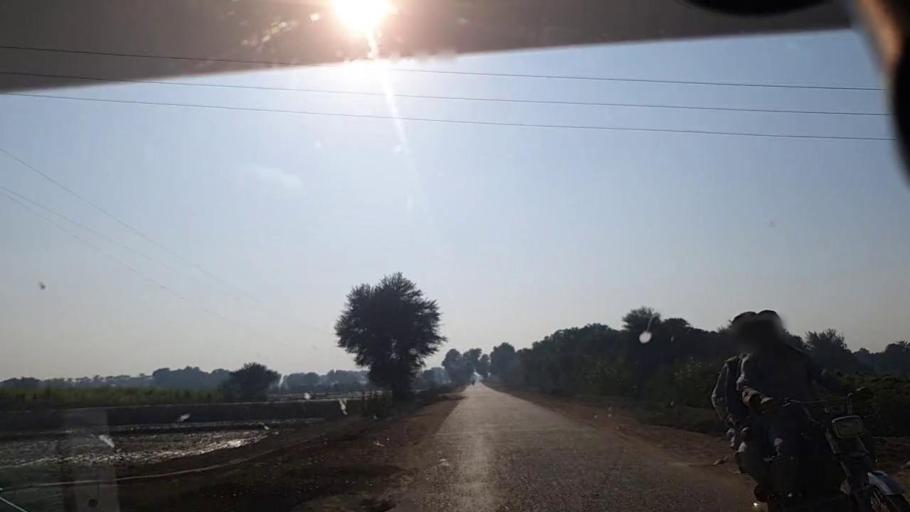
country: PK
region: Sindh
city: Sobhadero
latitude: 27.2490
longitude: 68.2947
